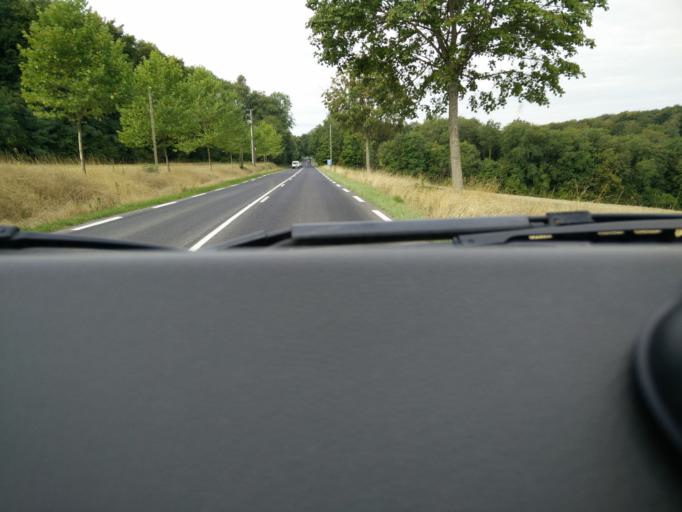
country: FR
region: Lorraine
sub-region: Departement de Meurthe-et-Moselle
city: Montauville
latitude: 48.9001
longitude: 6.0032
